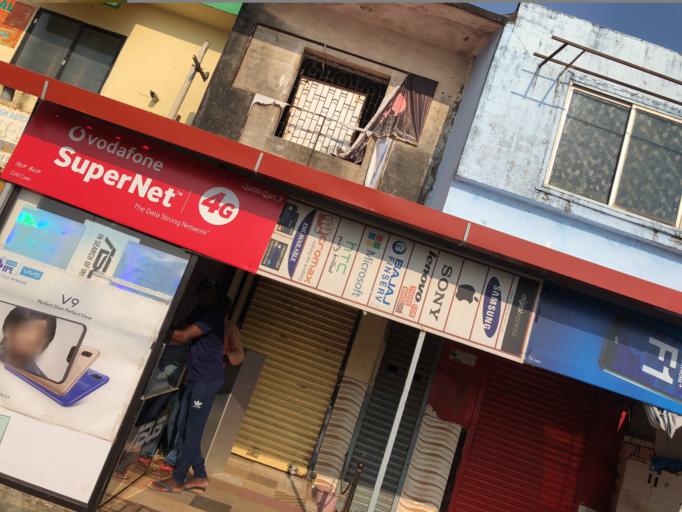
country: IN
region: Karnataka
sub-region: Dakshina Kannada
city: Mangalore
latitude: 12.8635
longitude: 74.8316
